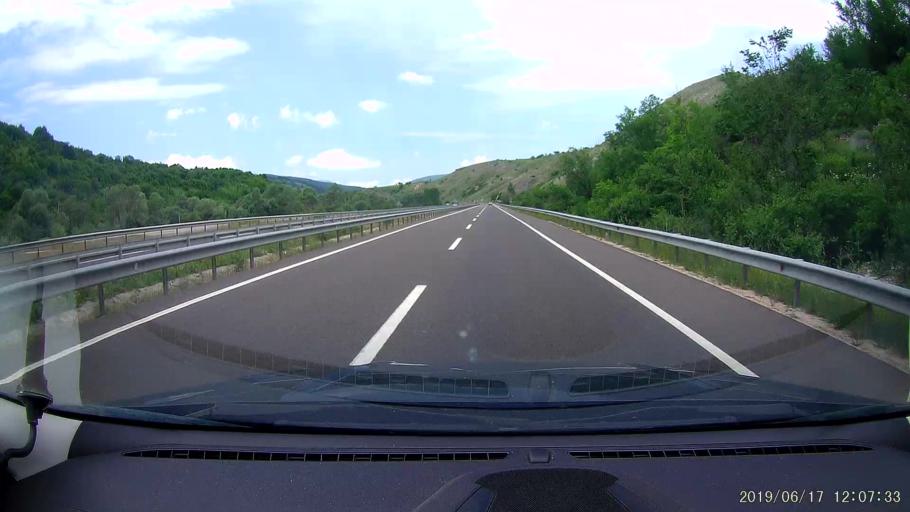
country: TR
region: Cankiri
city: Cerkes
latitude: 40.8340
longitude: 32.7299
